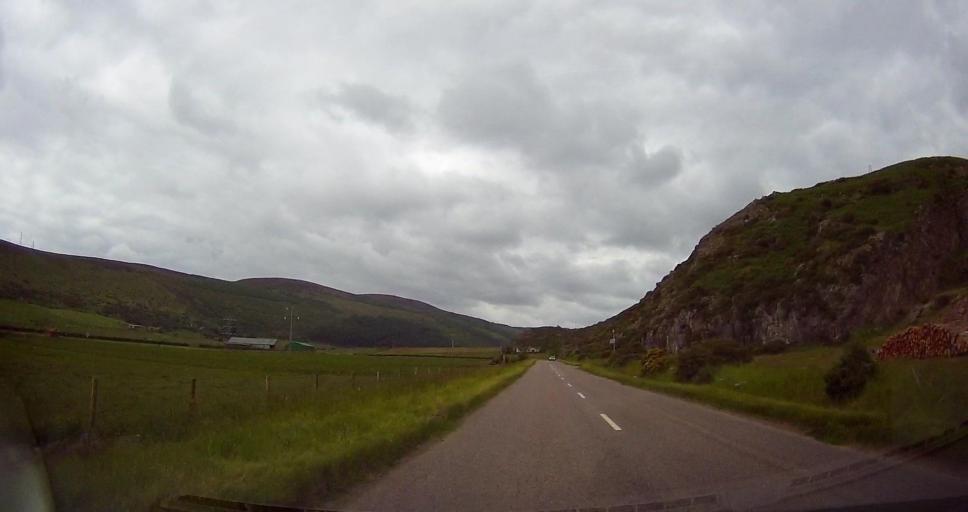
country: GB
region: Scotland
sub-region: Highland
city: Dornoch
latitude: 57.9828
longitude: -4.1254
